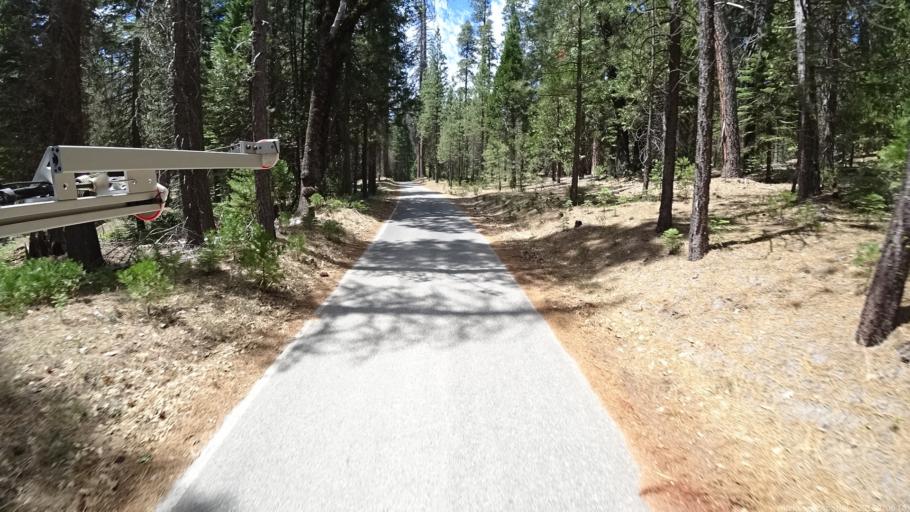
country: US
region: California
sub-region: Madera County
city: Oakhurst
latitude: 37.4110
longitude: -119.3861
